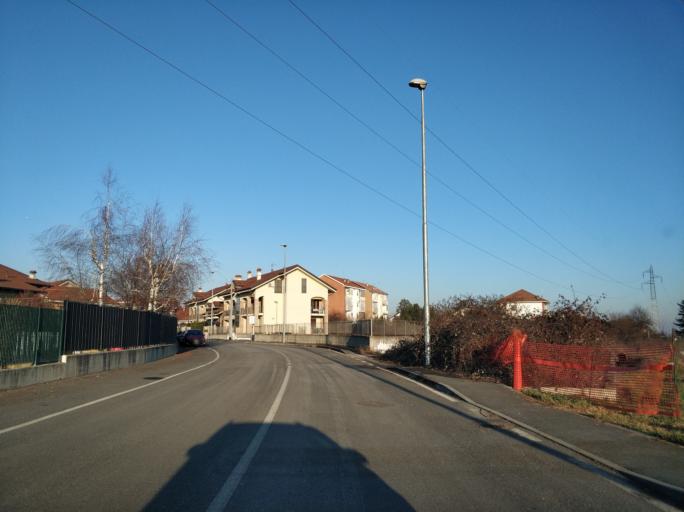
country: IT
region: Piedmont
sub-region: Provincia di Torino
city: San Maurizio
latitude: 45.2100
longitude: 7.6318
